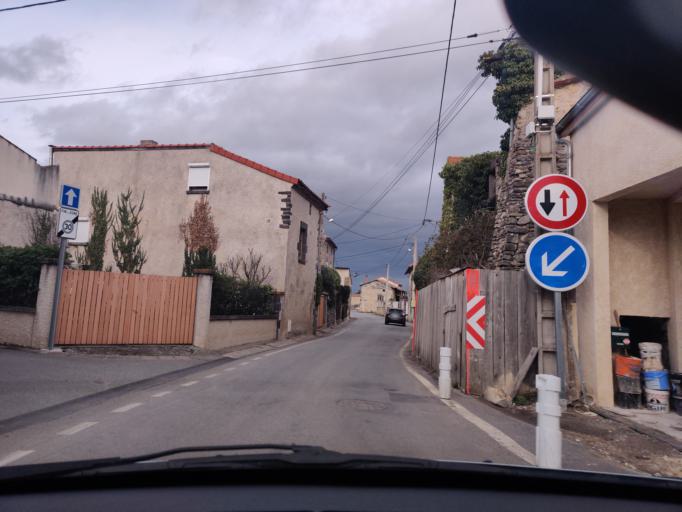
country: FR
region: Auvergne
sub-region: Departement du Puy-de-Dome
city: Saint-Bonnet-pres-Riom
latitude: 45.9335
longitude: 3.0919
